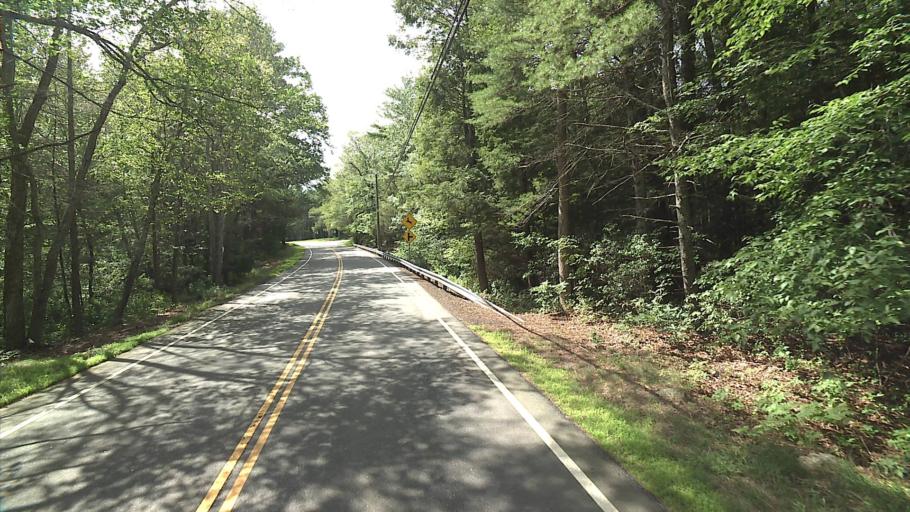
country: US
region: Massachusetts
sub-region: Hampden County
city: Holland
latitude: 41.9429
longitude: -72.1036
